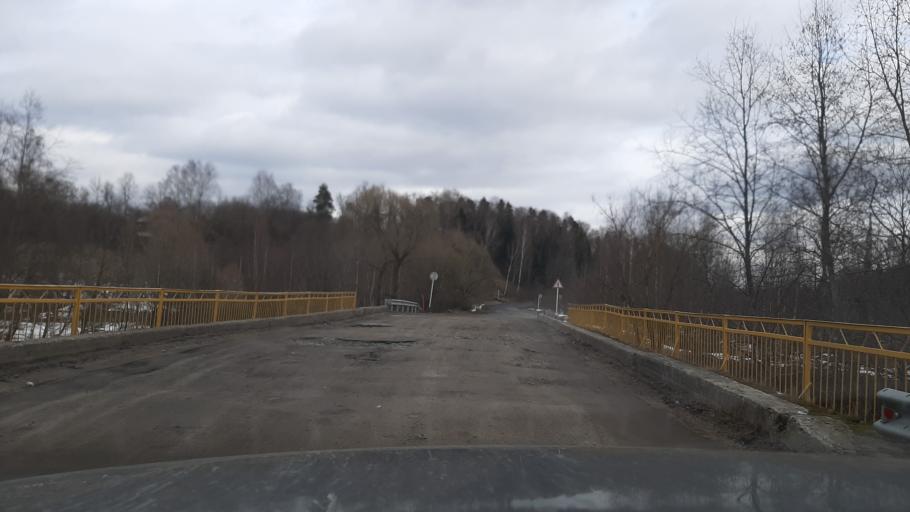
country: RU
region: Ivanovo
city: Teykovo
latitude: 56.8951
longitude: 40.6634
